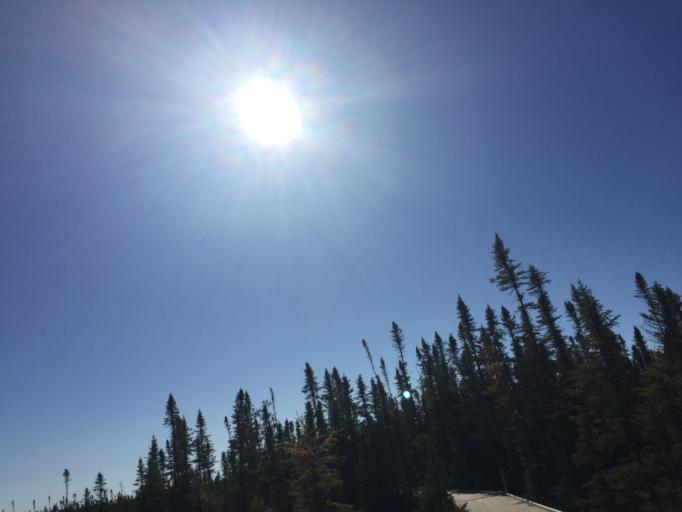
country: US
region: Minnesota
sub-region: Lake of the Woods County
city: Baudette
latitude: 48.2997
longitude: -94.5682
